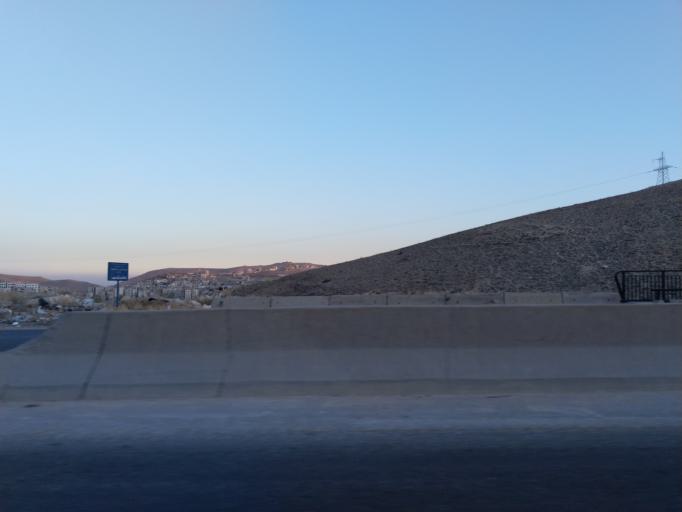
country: SY
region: Rif-dimashq
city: At Tall
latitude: 33.5848
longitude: 36.2901
